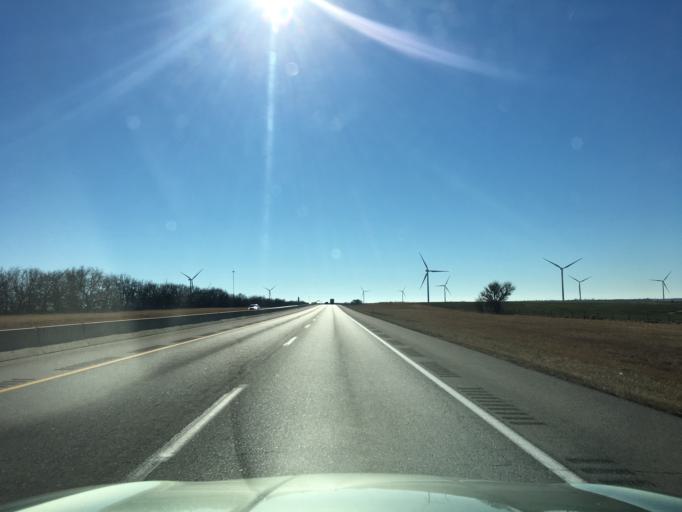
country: US
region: Kansas
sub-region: Sumner County
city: Wellington
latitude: 37.1566
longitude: -97.3395
